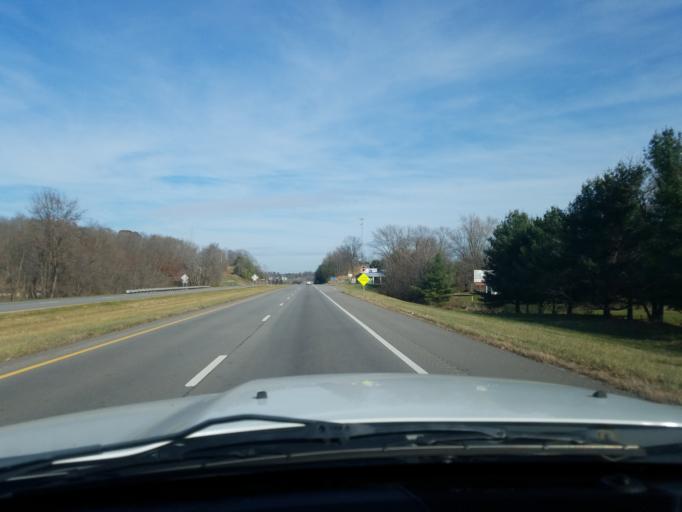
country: US
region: Ohio
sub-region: Athens County
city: Athens
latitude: 39.2420
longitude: -82.1883
